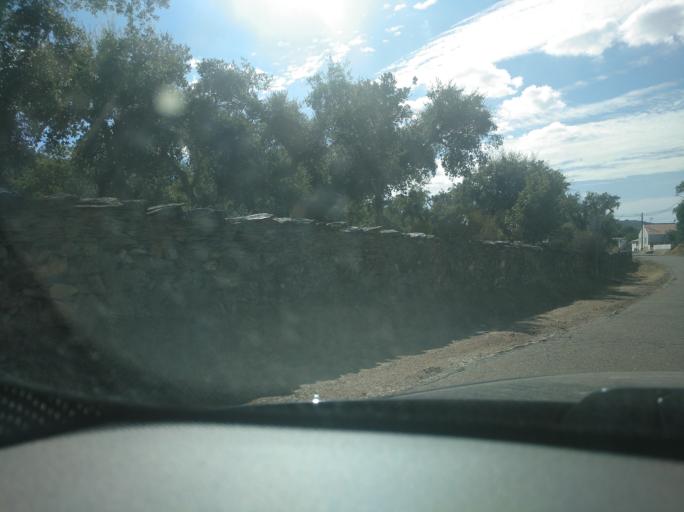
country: ES
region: Extremadura
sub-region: Provincia de Badajoz
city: La Codosera
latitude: 39.1551
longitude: -7.1708
